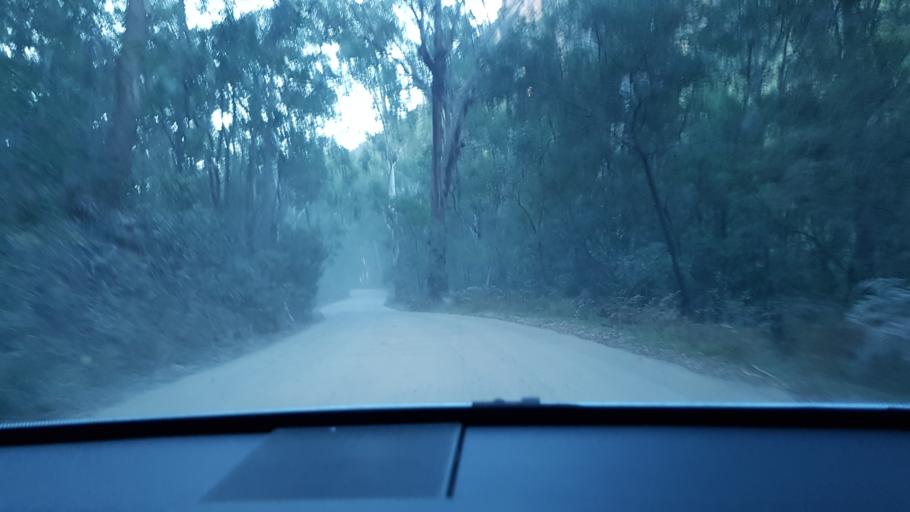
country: AU
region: New South Wales
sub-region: Lithgow
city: Portland
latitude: -33.1869
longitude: 150.2446
